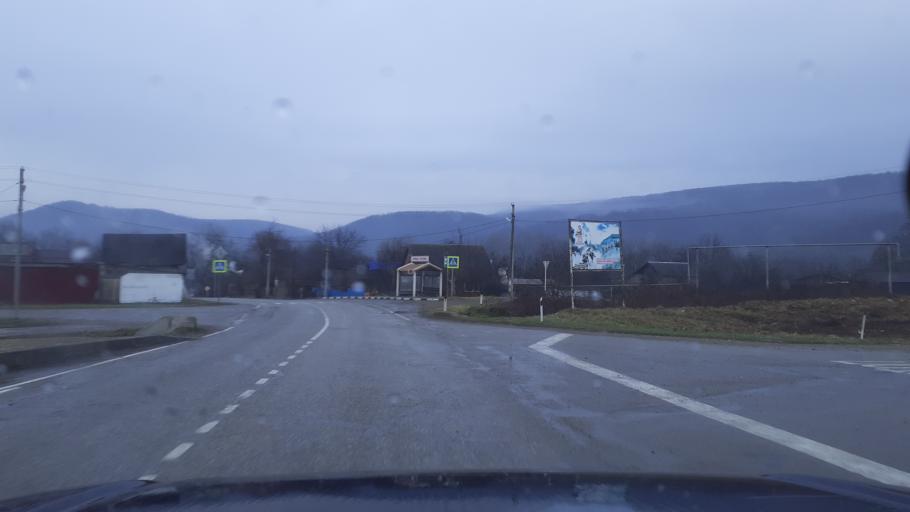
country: RU
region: Krasnodarskiy
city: Neftegorsk
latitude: 44.2938
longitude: 39.8262
